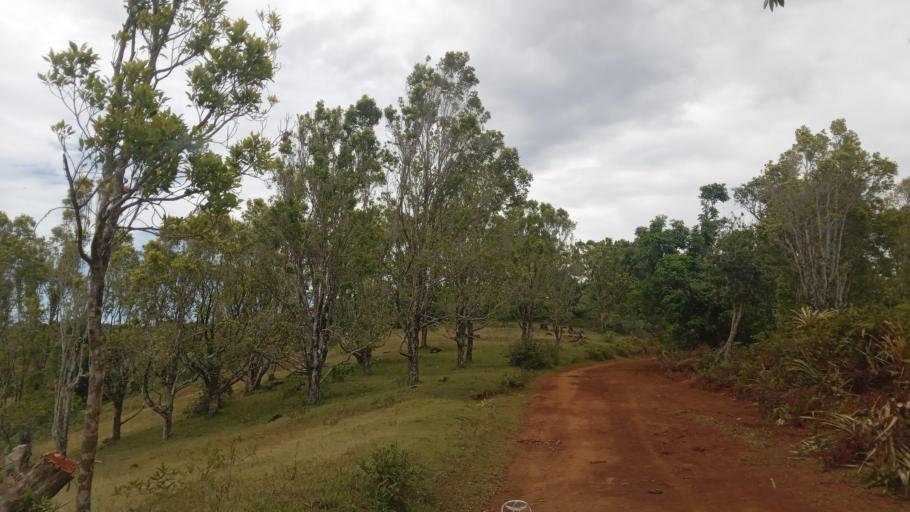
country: MG
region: Atsimo-Atsinanana
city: Vohipaho
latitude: -23.6165
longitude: 47.5818
